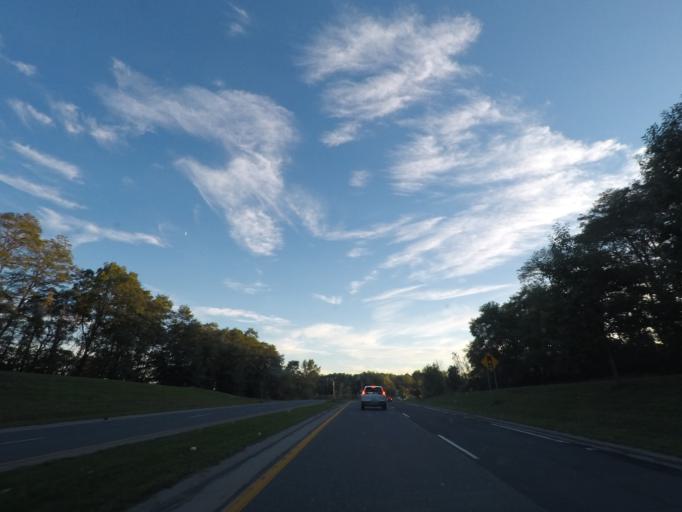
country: US
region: New York
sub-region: Albany County
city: Colonie
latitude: 42.7419
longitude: -73.8187
